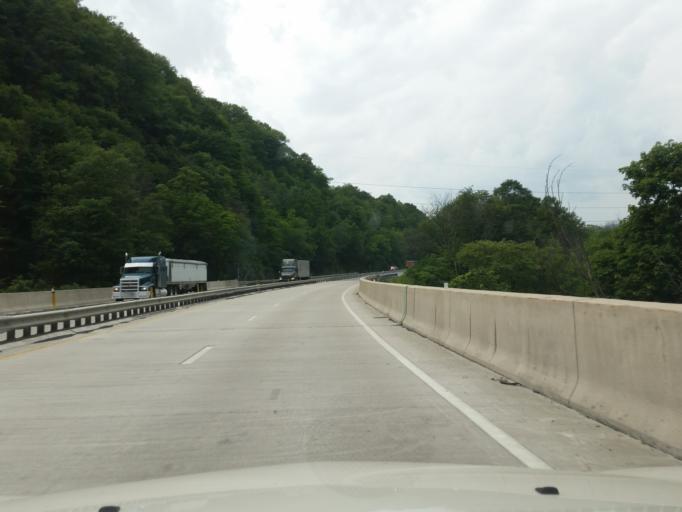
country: US
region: Pennsylvania
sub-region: Mifflin County
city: Yeagertown
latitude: 40.6561
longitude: -77.5921
